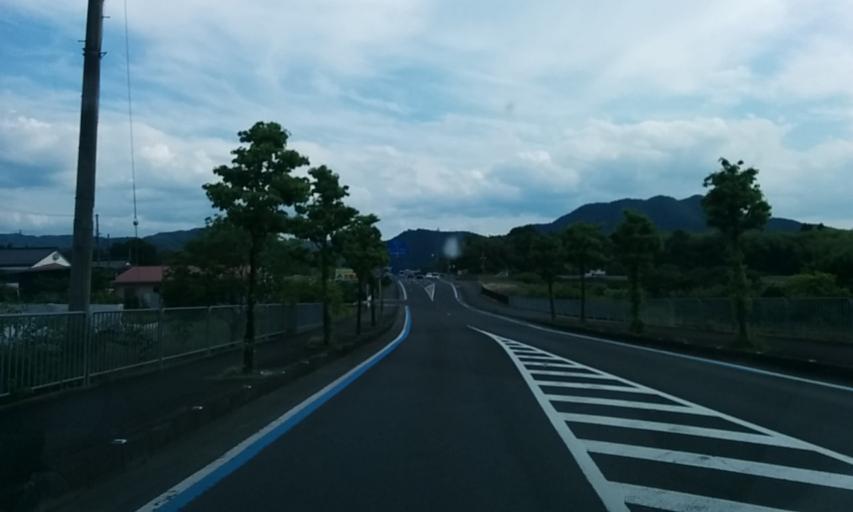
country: JP
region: Kyoto
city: Ayabe
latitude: 35.3133
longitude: 135.2596
